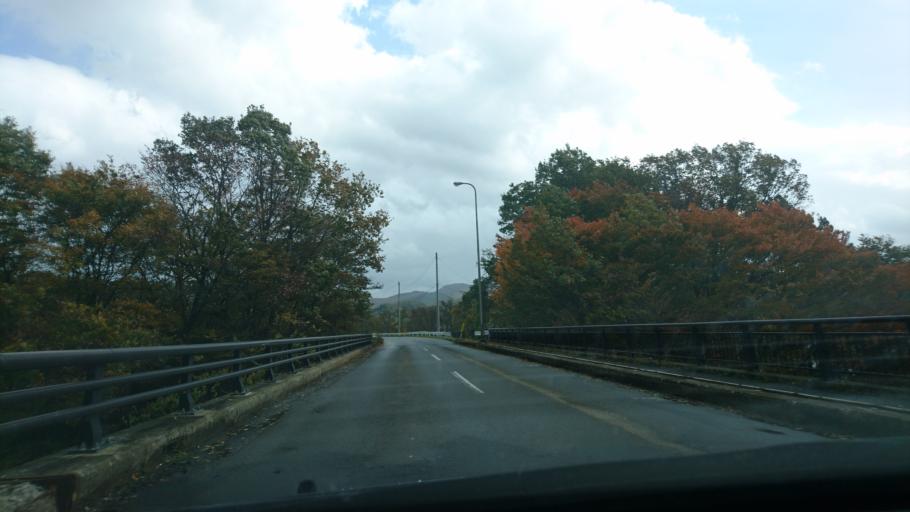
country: JP
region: Iwate
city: Shizukuishi
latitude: 39.6758
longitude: 140.9963
